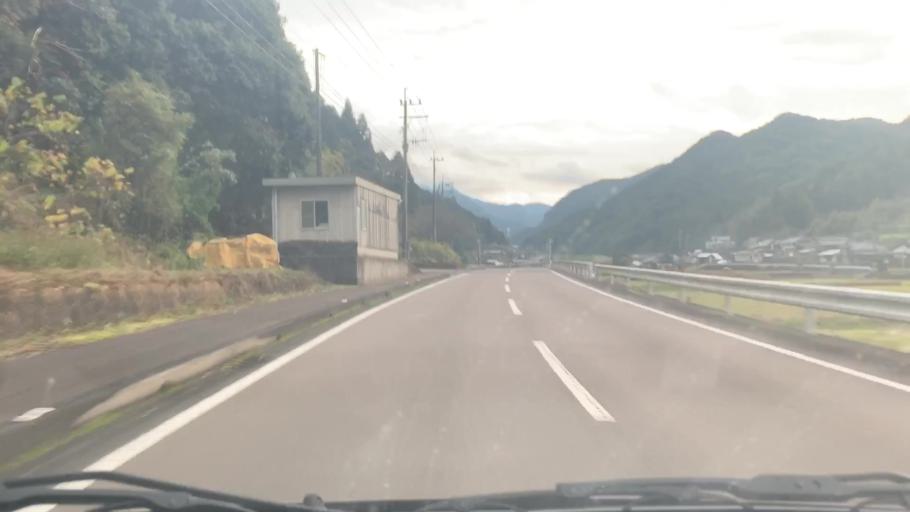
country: JP
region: Saga Prefecture
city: Kashima
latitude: 33.0672
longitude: 130.0703
